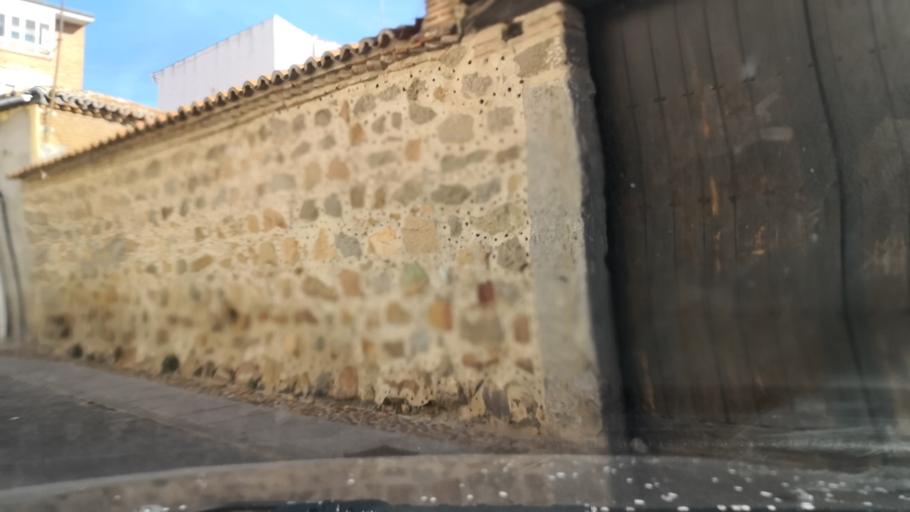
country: ES
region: Castille and Leon
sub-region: Provincia de Avila
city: Avila
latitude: 40.6519
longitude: -4.7004
